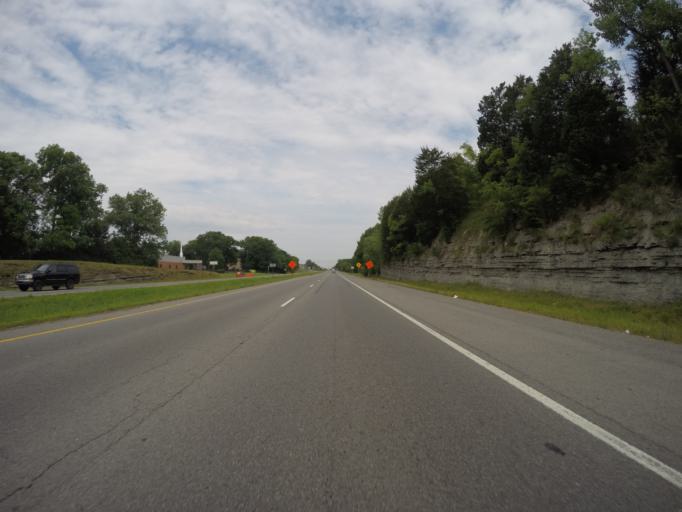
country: US
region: Tennessee
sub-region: Davidson County
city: Lakewood
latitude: 36.2637
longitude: -86.6854
